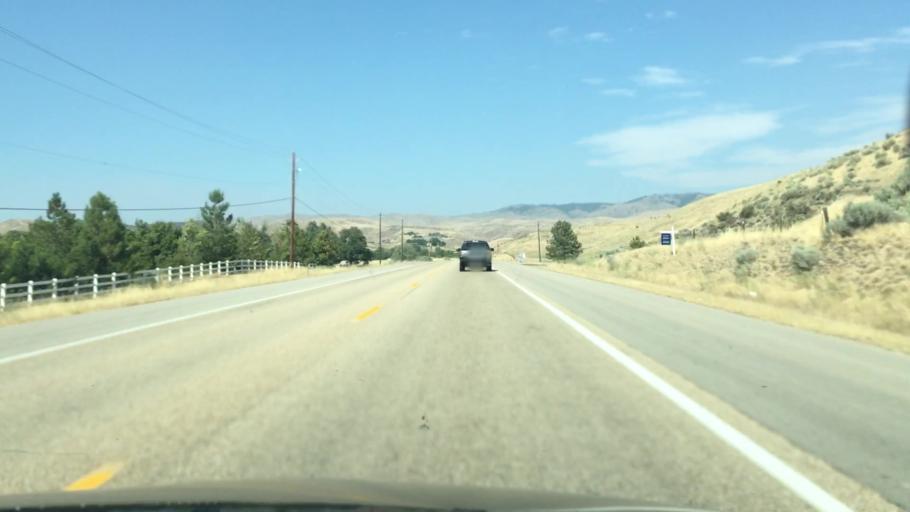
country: US
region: Idaho
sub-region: Ada County
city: Eagle
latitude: 43.7252
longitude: -116.3126
